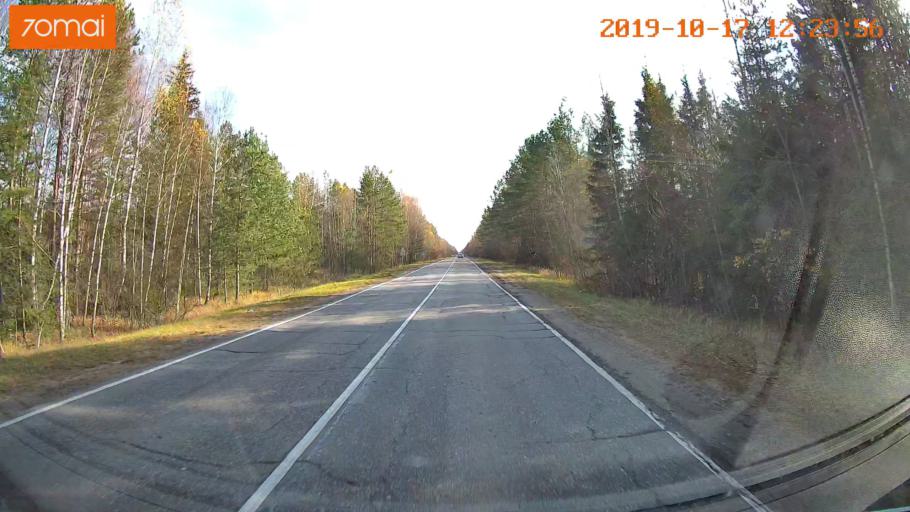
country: RU
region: Rjazan
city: Gus'-Zheleznyy
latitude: 55.0398
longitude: 41.2041
